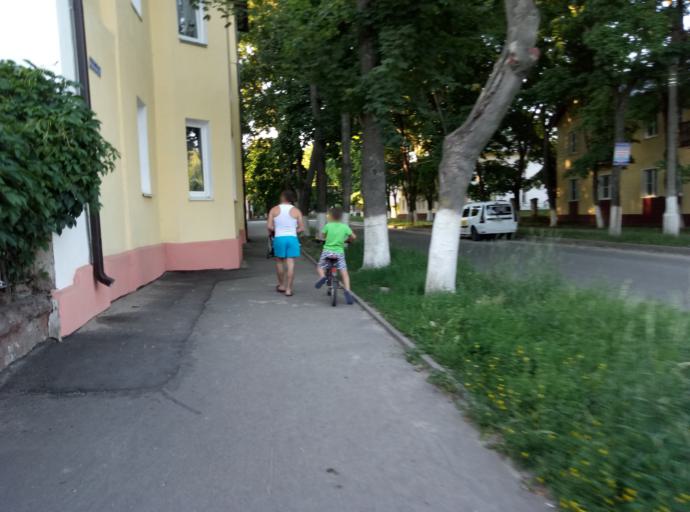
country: RU
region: Kursk
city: Kursk
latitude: 51.6723
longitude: 36.1517
